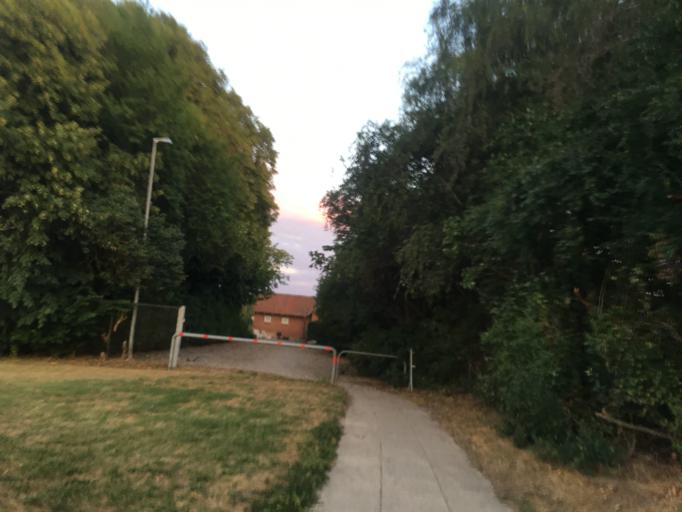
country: DK
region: Central Jutland
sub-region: Syddjurs Kommune
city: Hornslet
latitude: 56.3176
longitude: 10.3242
